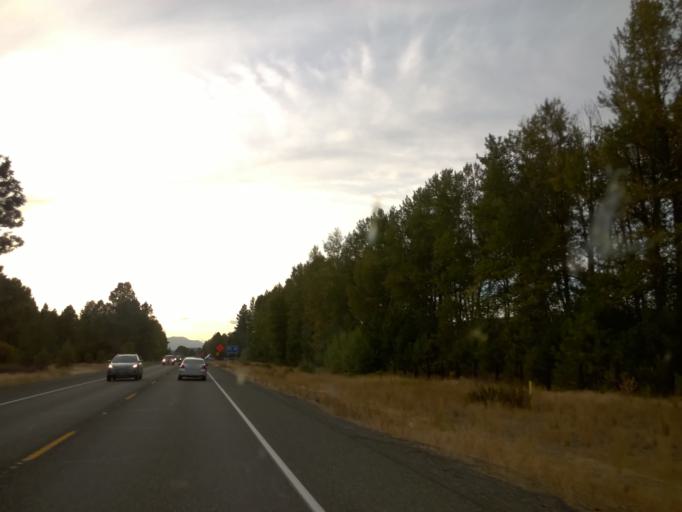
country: US
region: Washington
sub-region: Kittitas County
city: Cle Elum
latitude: 47.1836
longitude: -120.8868
